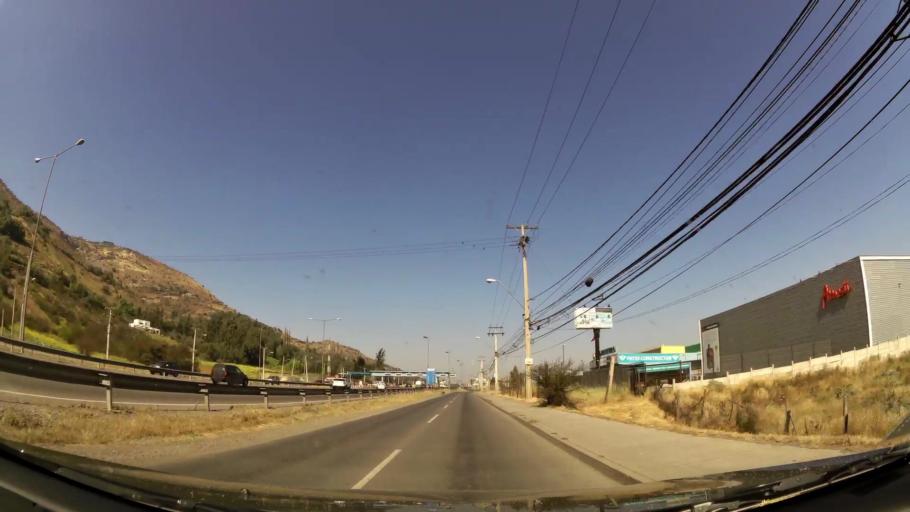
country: CL
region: Santiago Metropolitan
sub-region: Provincia de Chacabuco
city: Chicureo Abajo
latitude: -33.3090
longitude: -70.7015
